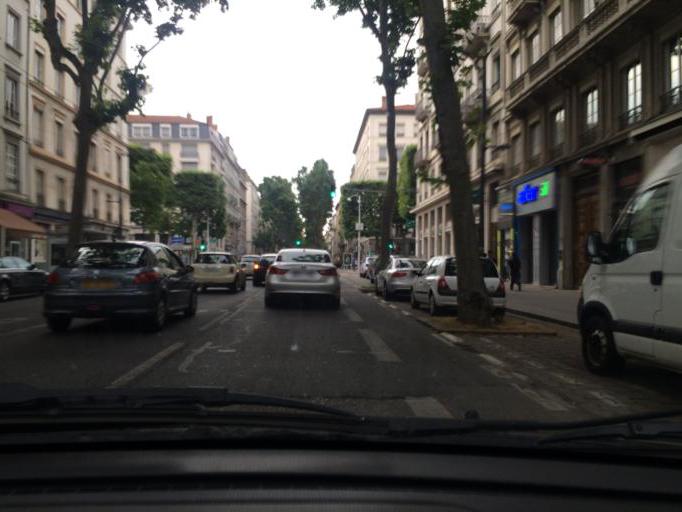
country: FR
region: Rhone-Alpes
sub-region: Departement du Rhone
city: Lyon
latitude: 45.7679
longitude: 4.8441
